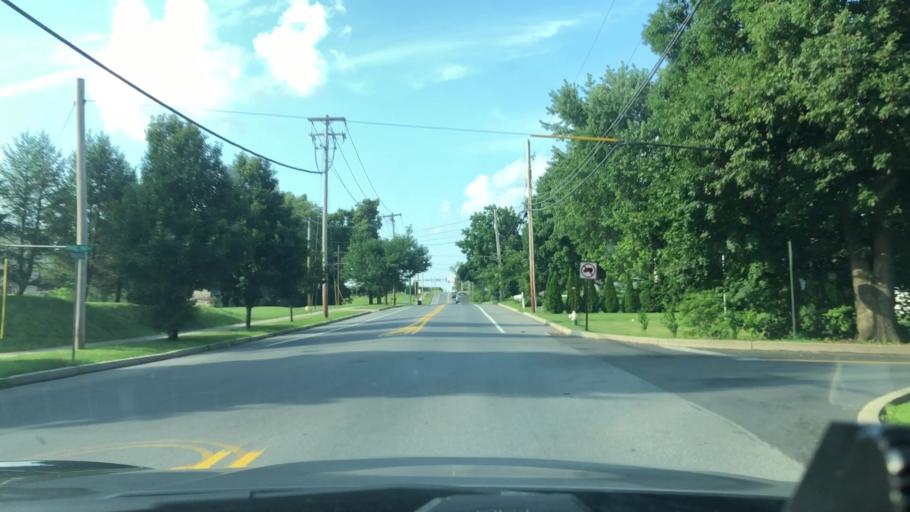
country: US
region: Pennsylvania
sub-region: Lehigh County
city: Wescosville
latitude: 40.6083
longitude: -75.5636
